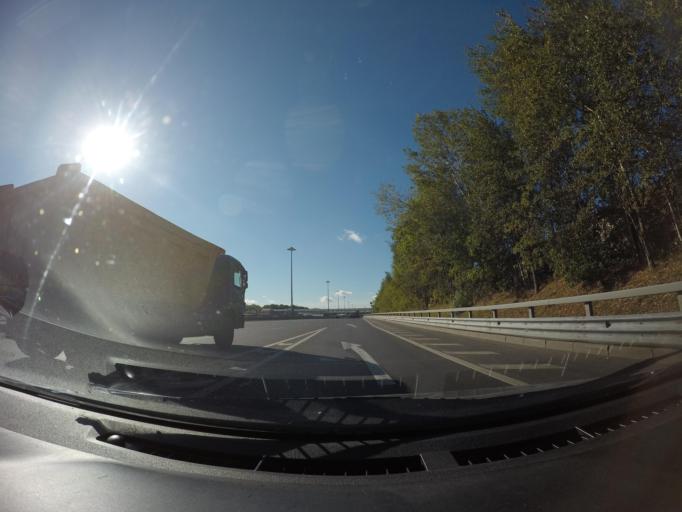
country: RU
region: Moscow
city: Ryazanskiy
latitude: 55.7728
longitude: 37.7458
